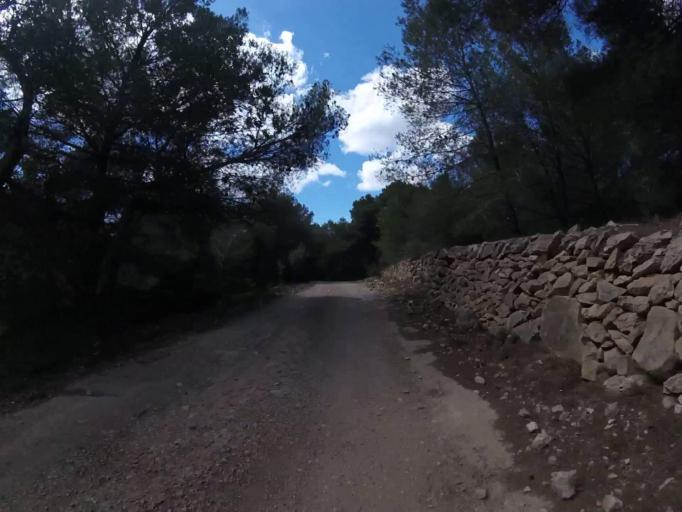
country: ES
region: Valencia
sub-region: Provincia de Castello
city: Santa Magdalena de Pulpis
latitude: 40.3164
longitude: 0.3310
